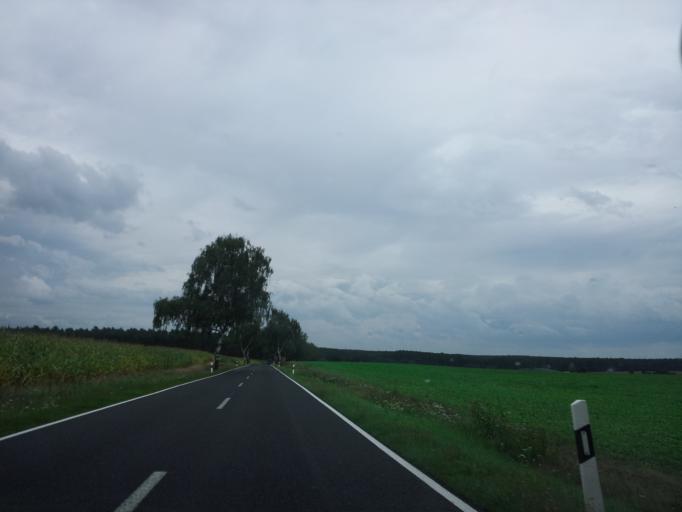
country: DE
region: Brandenburg
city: Gorzke
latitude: 52.1733
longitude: 12.3952
